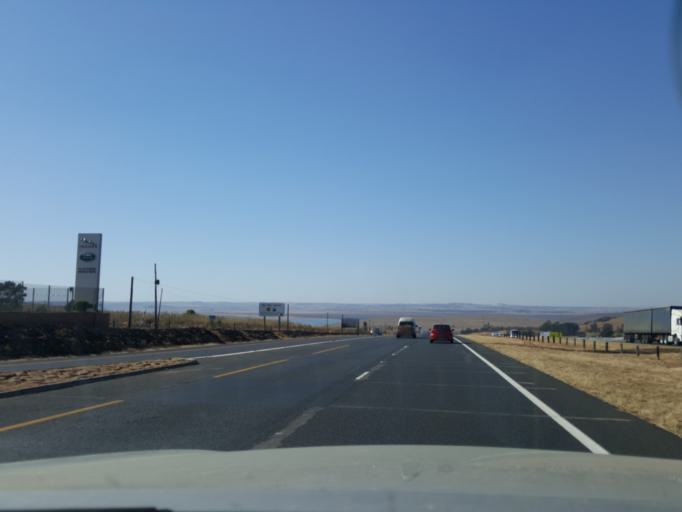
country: ZA
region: Mpumalanga
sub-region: Nkangala District Municipality
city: Witbank
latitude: -25.8866
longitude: 29.2733
